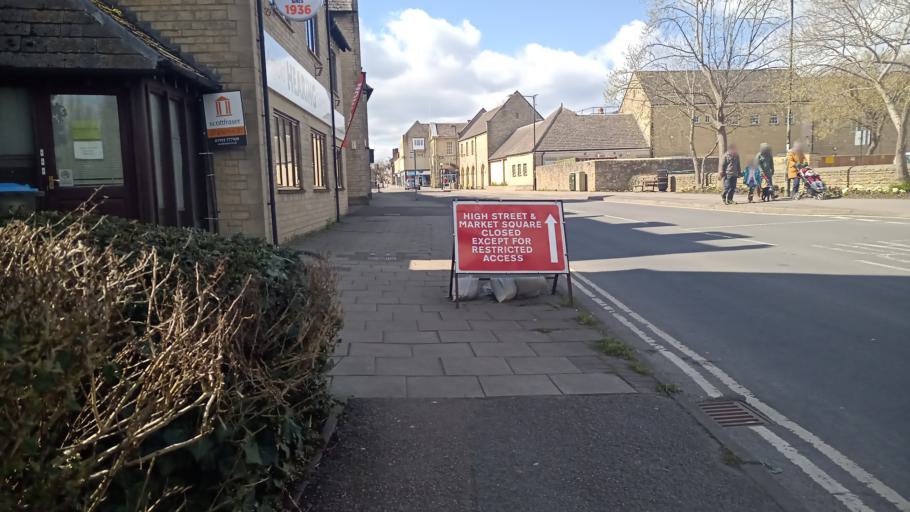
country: GB
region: England
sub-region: Oxfordshire
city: Witney
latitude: 51.7838
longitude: -1.4834
